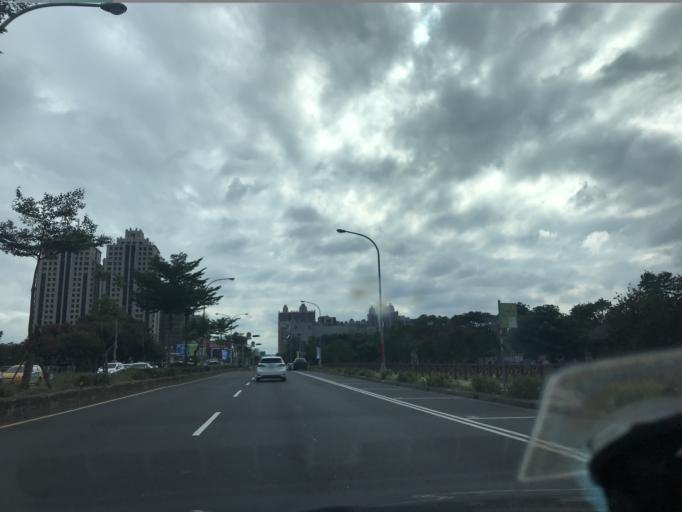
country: TW
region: Taiwan
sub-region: Hsinchu
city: Zhubei
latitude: 24.8249
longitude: 121.0240
